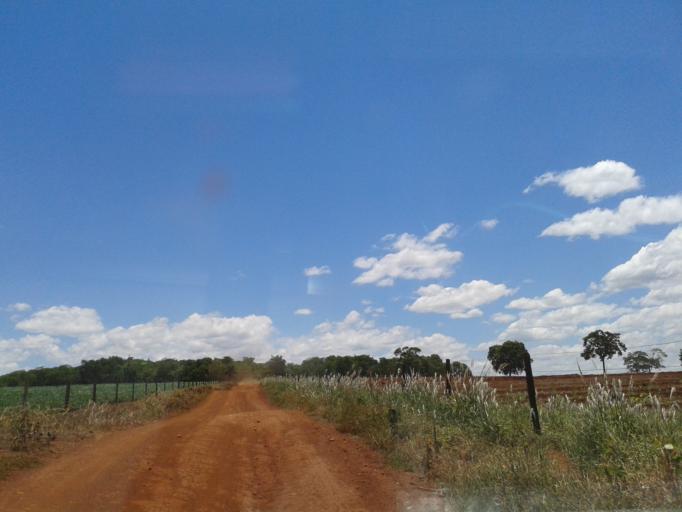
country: BR
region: Minas Gerais
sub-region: Centralina
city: Centralina
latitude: -18.6807
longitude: -49.2265
